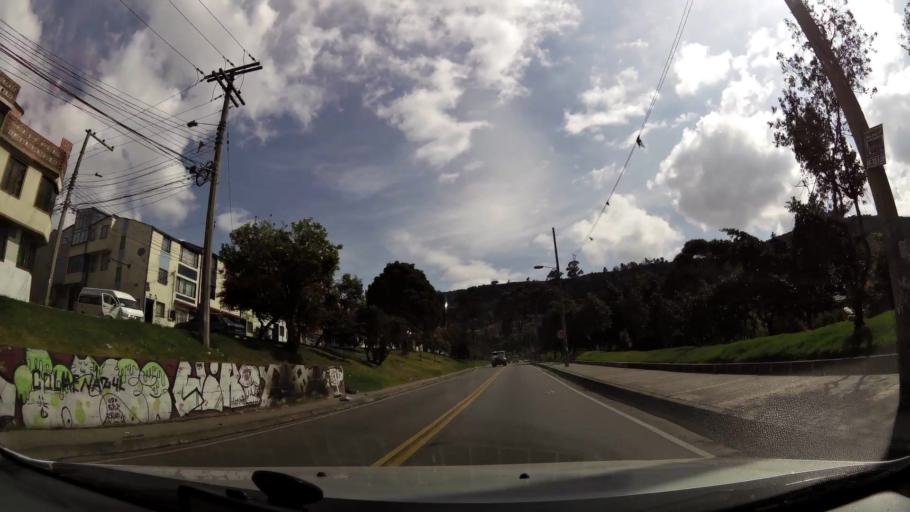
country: CO
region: Bogota D.C.
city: Bogota
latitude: 4.5619
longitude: -74.1031
